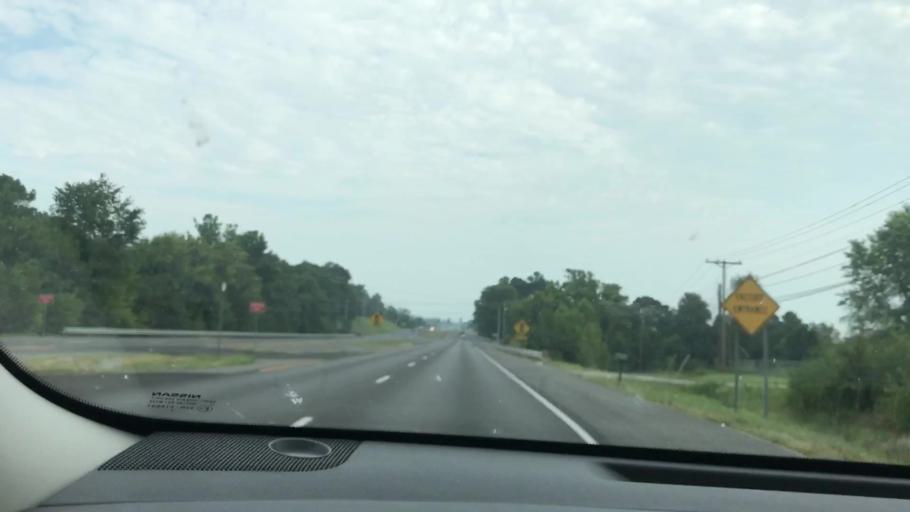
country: US
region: Kentucky
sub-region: Calloway County
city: Murray
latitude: 36.6442
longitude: -88.3083
